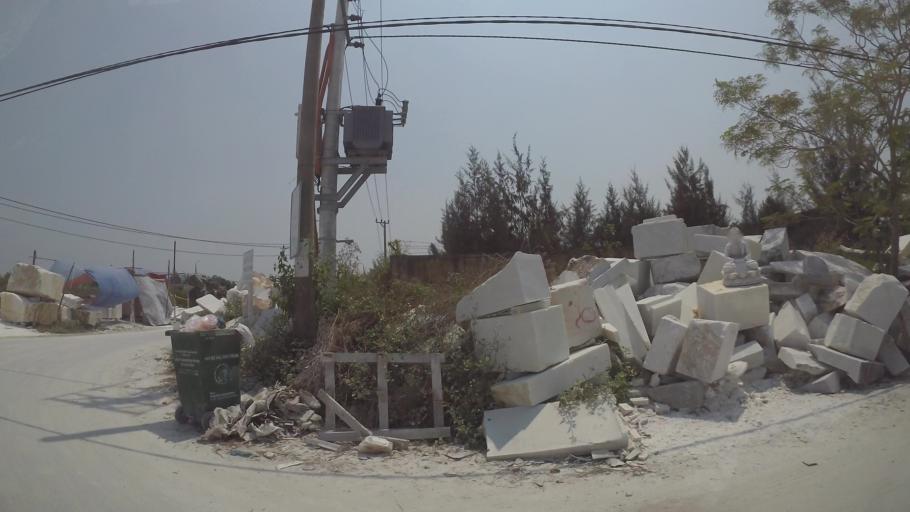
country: VN
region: Da Nang
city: Ngu Hanh Son
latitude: 15.9907
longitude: 108.2530
